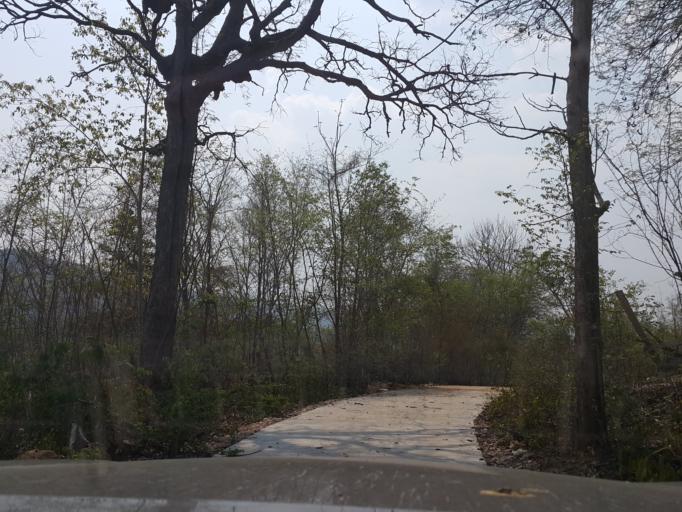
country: TH
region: Lampang
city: Mae Phrik
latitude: 17.5277
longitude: 98.9967
